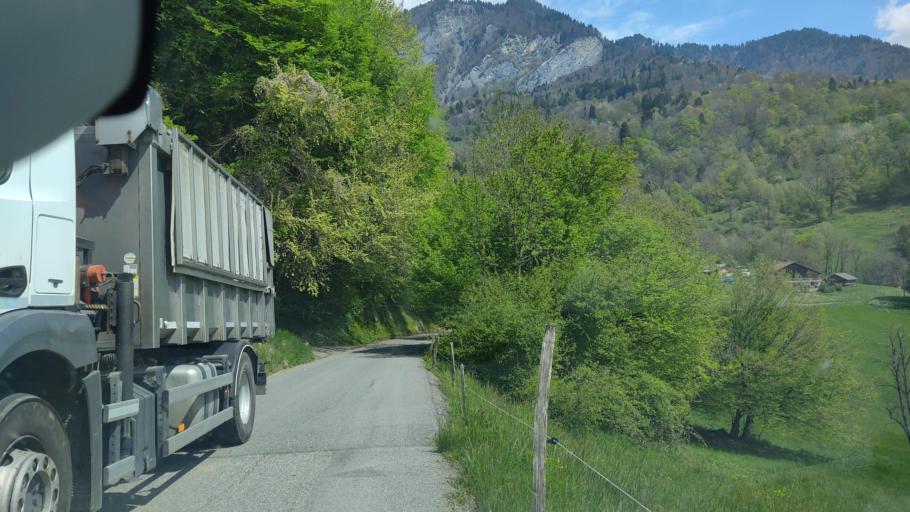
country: FR
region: Rhone-Alpes
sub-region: Departement de la Savoie
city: Ugine
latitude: 45.7662
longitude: 6.4113
